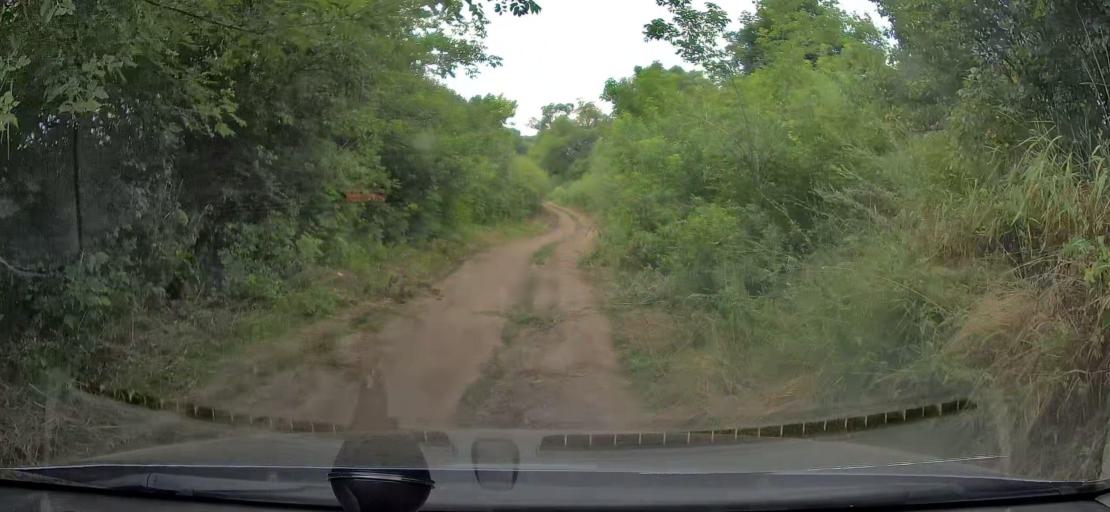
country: RU
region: Kursk
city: Zolotukhino
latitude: 52.0263
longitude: 36.2038
